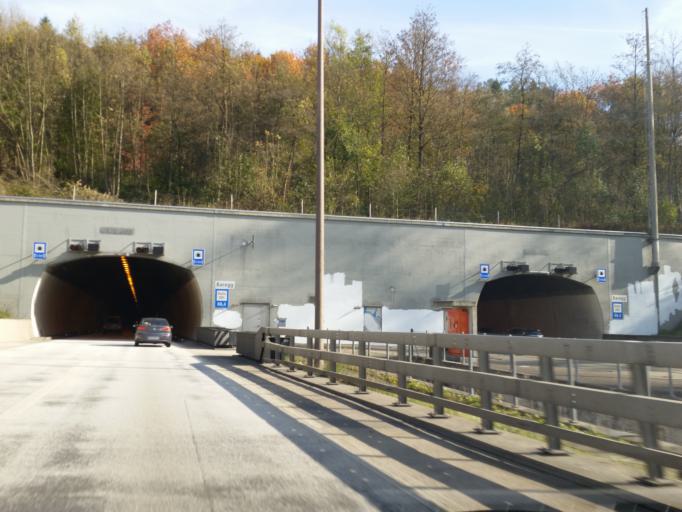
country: CH
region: Aargau
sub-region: Bezirk Baden
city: Baden
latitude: 47.4588
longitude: 8.2883
